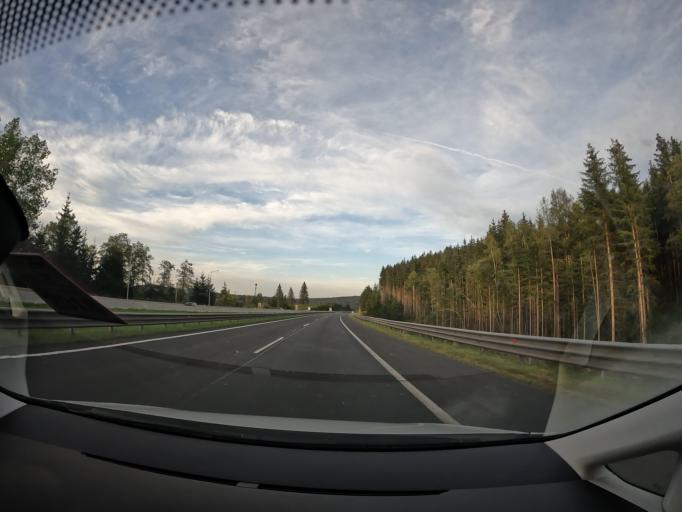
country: AT
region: Styria
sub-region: Politischer Bezirk Voitsberg
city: Pack
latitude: 46.9559
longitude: 15.0122
